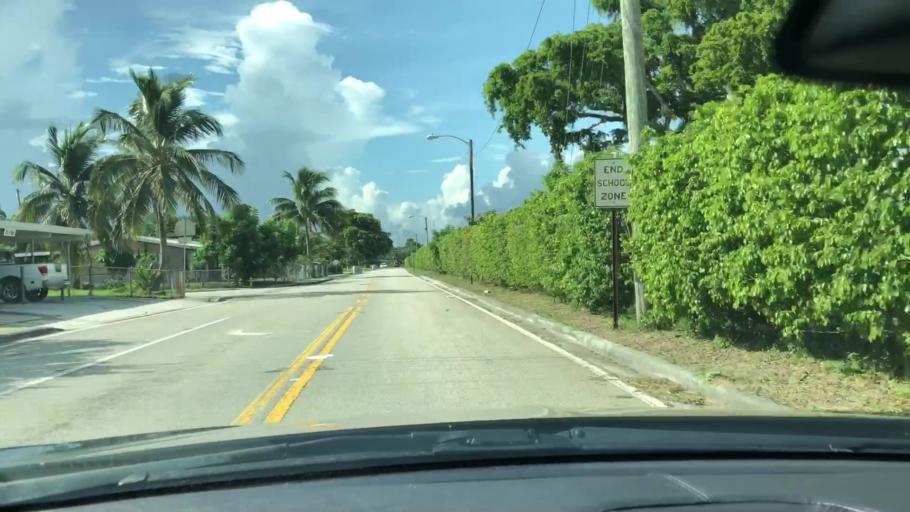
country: US
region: Florida
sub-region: Broward County
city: Kendall Green
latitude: 26.2604
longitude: -80.1230
